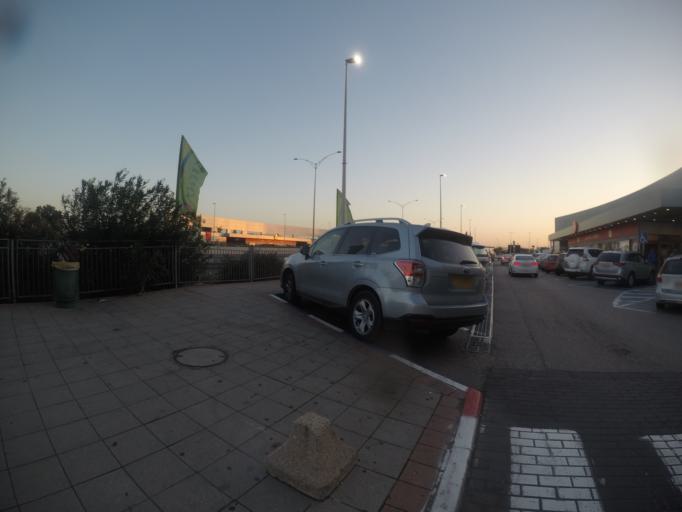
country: PS
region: West Bank
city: Zayta
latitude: 32.3812
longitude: 35.0174
